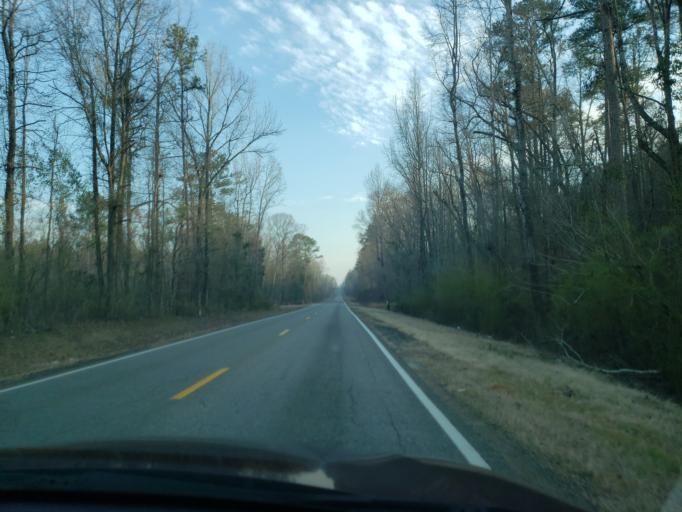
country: US
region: Alabama
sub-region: Hale County
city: Greensboro
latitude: 32.8023
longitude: -87.5930
